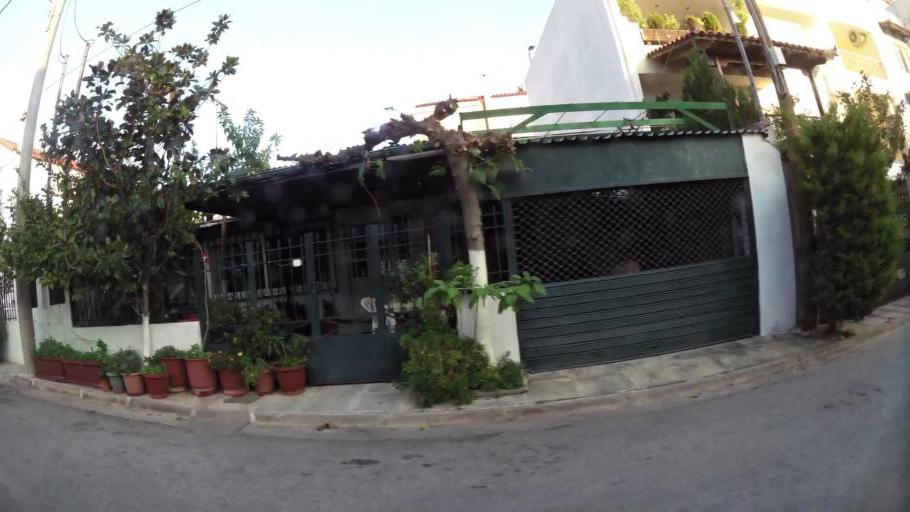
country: GR
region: Attica
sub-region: Nomarchia Anatolikis Attikis
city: Acharnes
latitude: 38.0975
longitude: 23.7437
